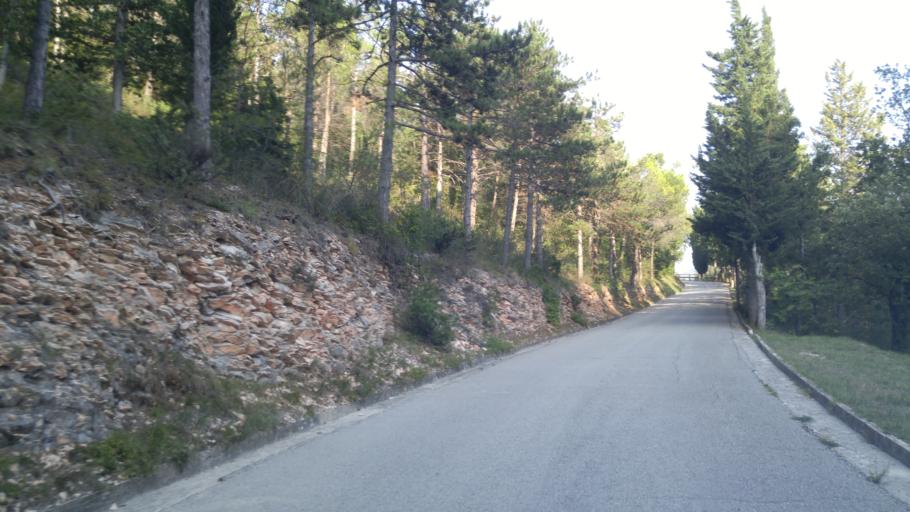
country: IT
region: The Marches
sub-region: Provincia di Pesaro e Urbino
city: Acqualagna
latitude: 43.6203
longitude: 12.6686
